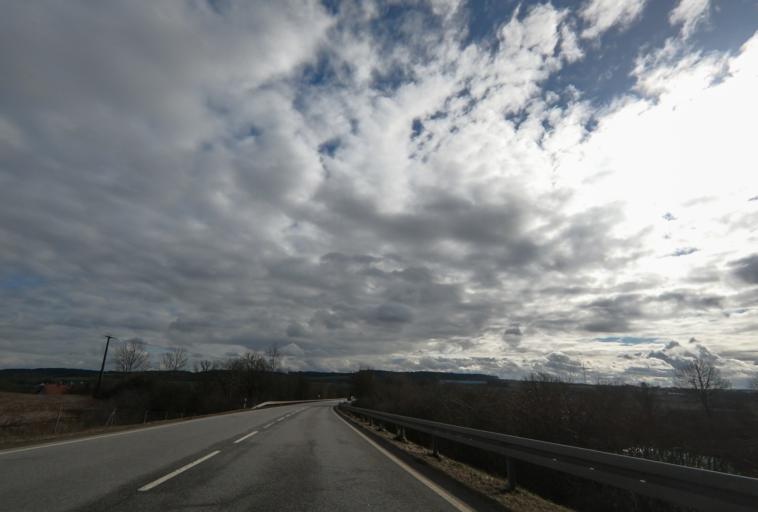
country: DE
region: Bavaria
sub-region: Lower Bavaria
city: Mallersdorf-Pfaffenberg
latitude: 48.7589
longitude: 12.2016
